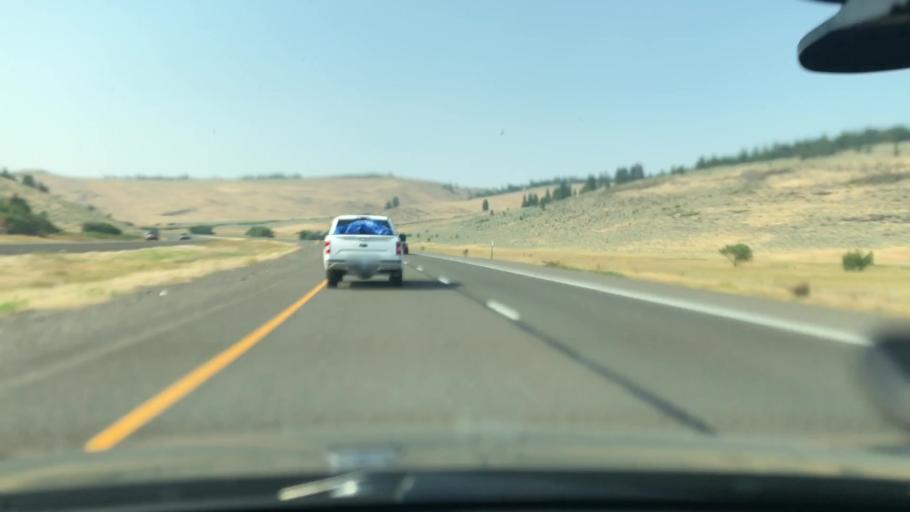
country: US
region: Oregon
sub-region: Union County
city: Union
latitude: 45.1629
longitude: -117.9641
